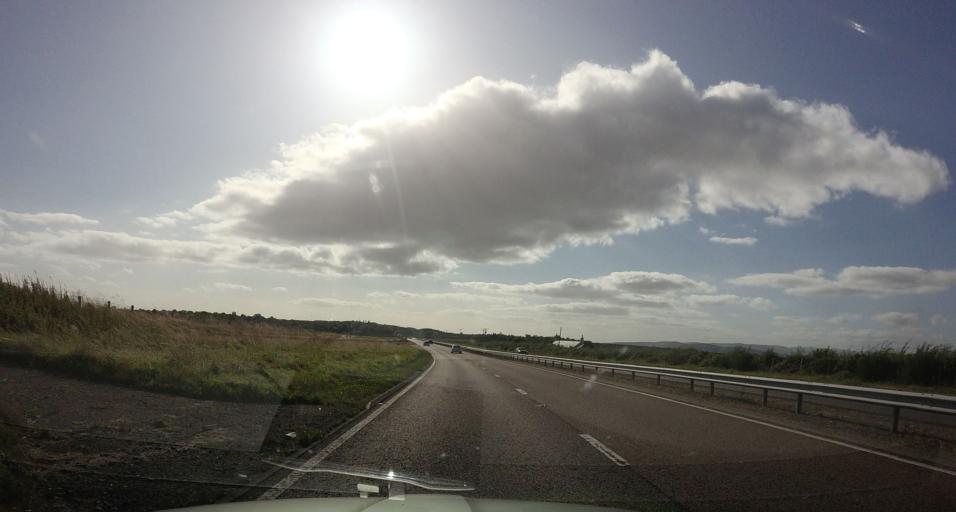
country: GB
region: Scotland
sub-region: Aberdeenshire
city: Laurencekirk
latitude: 56.8066
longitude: -2.5255
